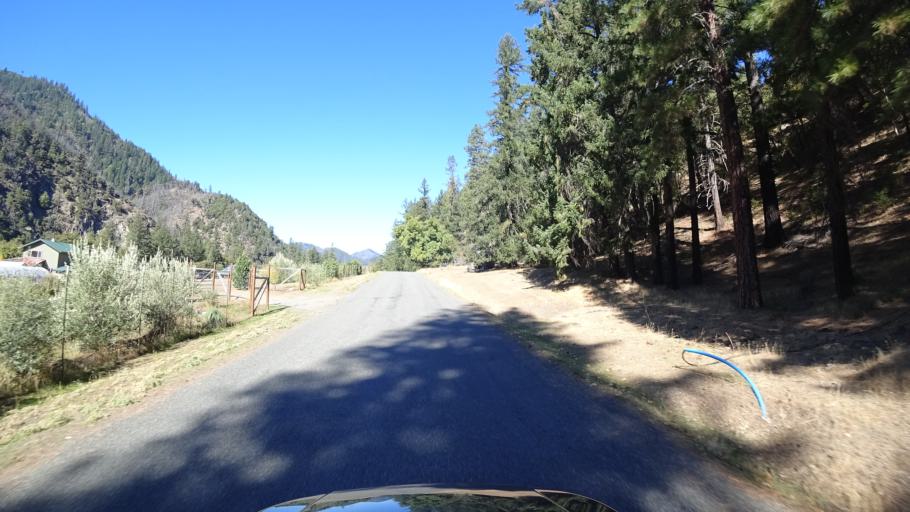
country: US
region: California
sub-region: Humboldt County
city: Willow Creek
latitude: 41.2667
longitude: -123.3357
